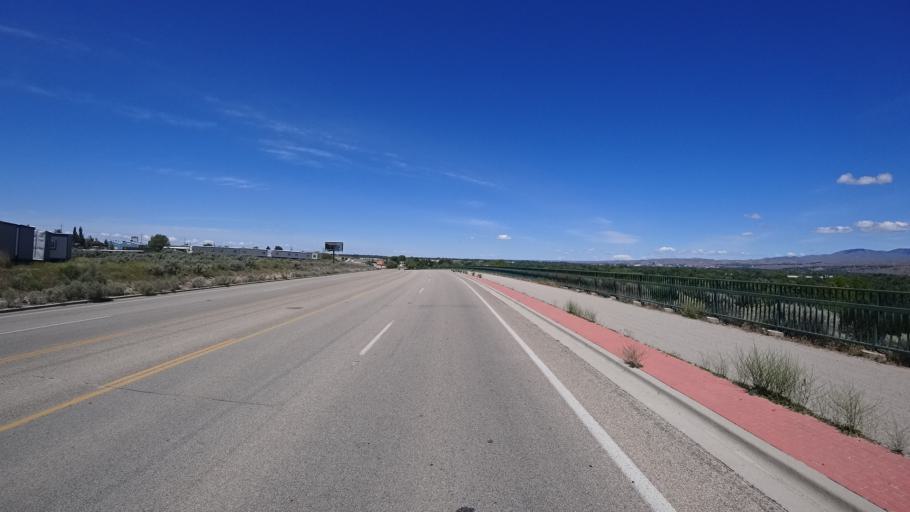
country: US
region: Idaho
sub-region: Ada County
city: Boise
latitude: 43.5636
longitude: -116.1736
